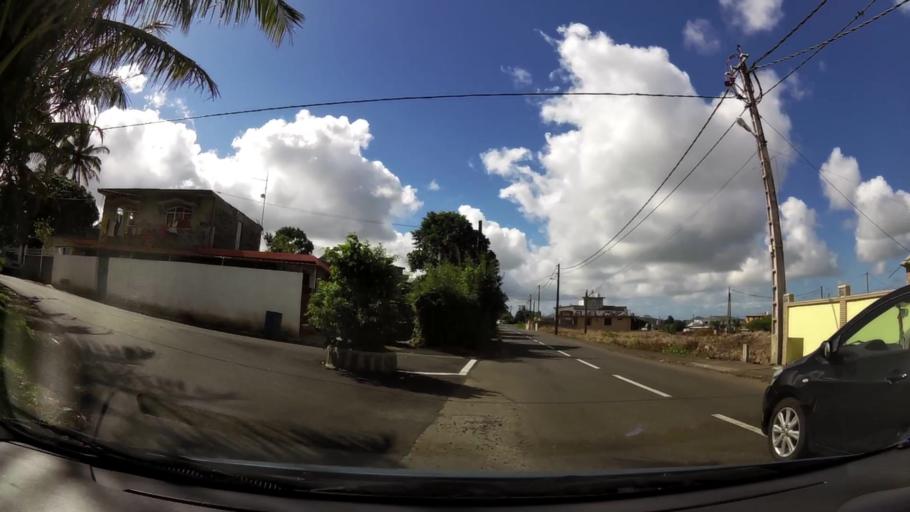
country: MU
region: Grand Port
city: Rose Belle
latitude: -20.3972
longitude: 57.5902
